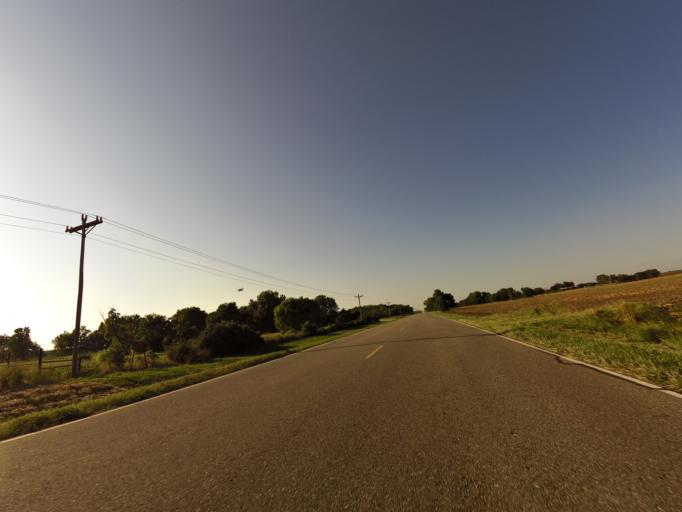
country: US
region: Kansas
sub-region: Reno County
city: Buhler
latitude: 38.1664
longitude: -97.8487
